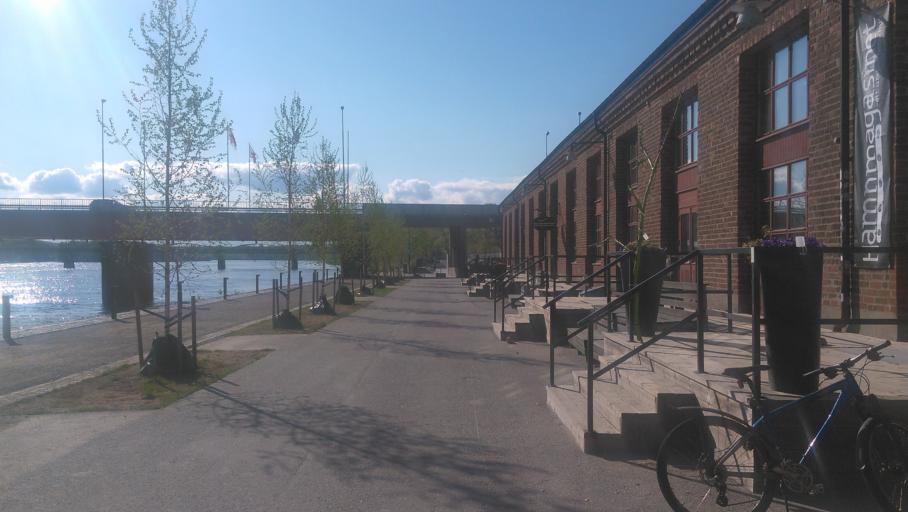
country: SE
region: Vaesterbotten
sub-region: Umea Kommun
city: Umea
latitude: 63.8249
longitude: 20.2568
